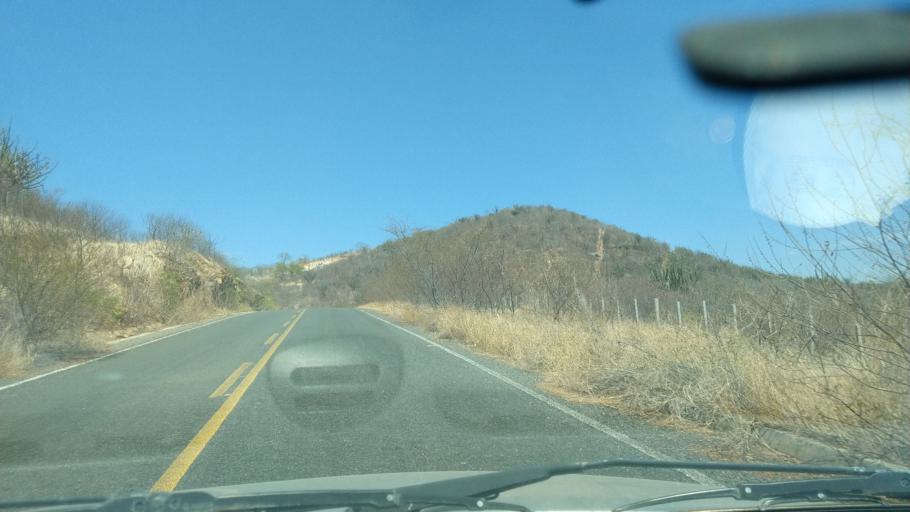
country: BR
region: Rio Grande do Norte
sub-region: Sao Tome
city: Sao Tome
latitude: -5.9685
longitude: -36.1555
